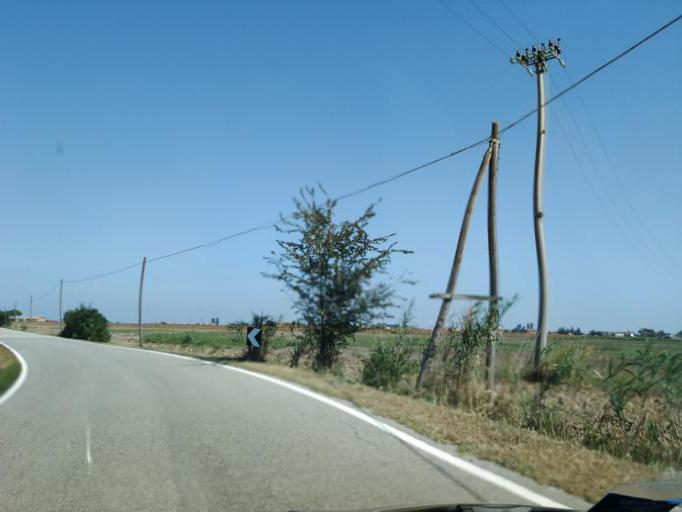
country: IT
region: Emilia-Romagna
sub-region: Provincia di Ferrara
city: Coccanile-Cesta
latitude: 44.8960
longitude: 11.9020
